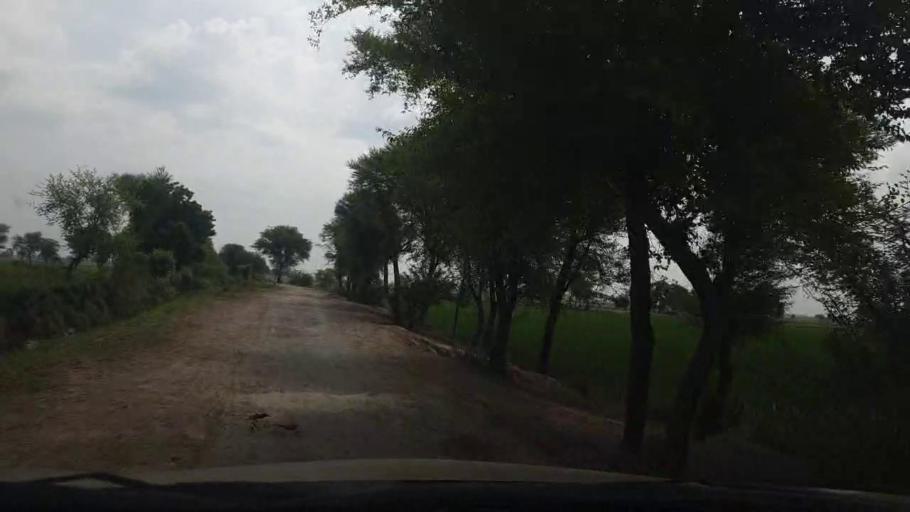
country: PK
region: Sindh
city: Larkana
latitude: 27.6840
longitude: 68.2001
